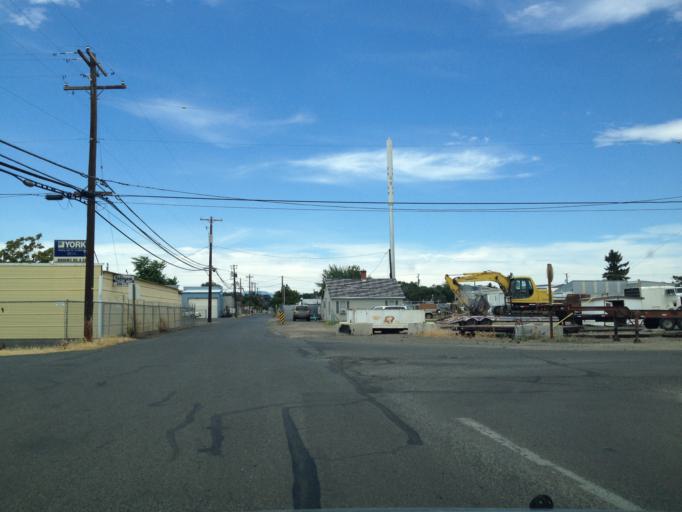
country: US
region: Washington
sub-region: Yakima County
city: Yakima
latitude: 46.6071
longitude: -120.5327
